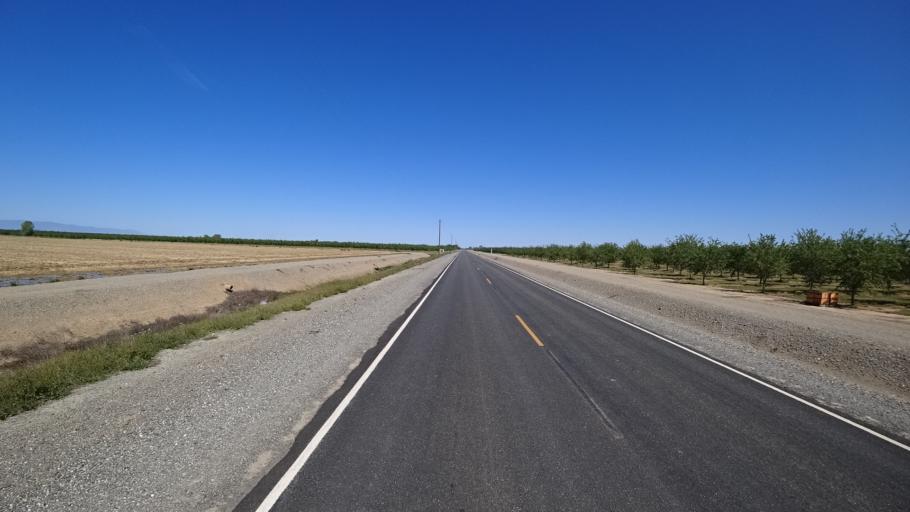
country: US
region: California
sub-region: Glenn County
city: Orland
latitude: 39.6583
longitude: -122.1408
